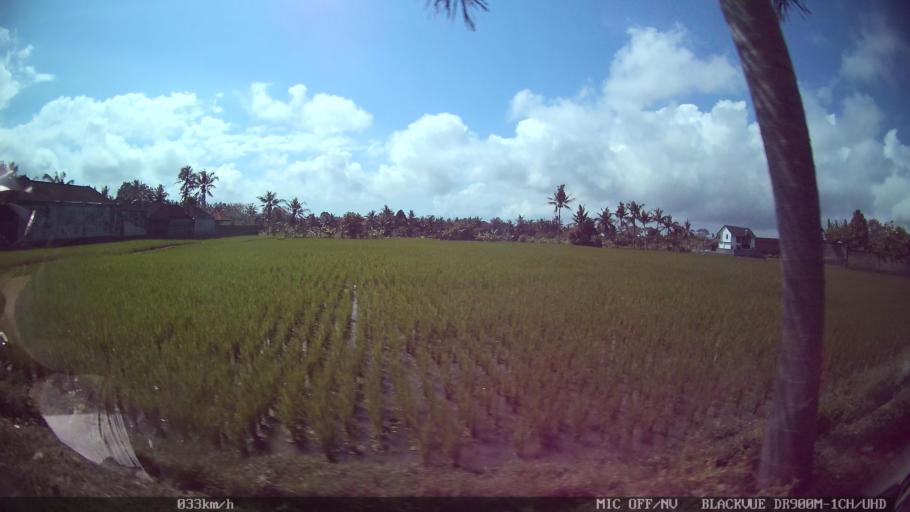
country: ID
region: Bali
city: Banjar Tebongkang
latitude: -8.5519
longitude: 115.2691
